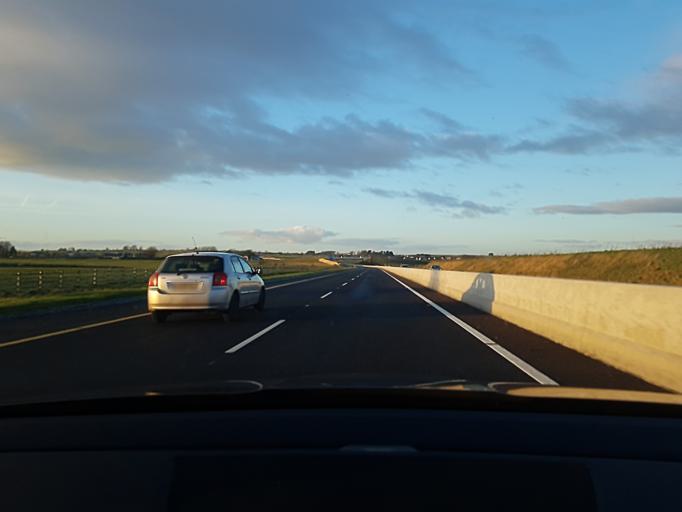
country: IE
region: Connaught
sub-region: County Galway
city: Athenry
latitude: 53.3881
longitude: -8.8014
